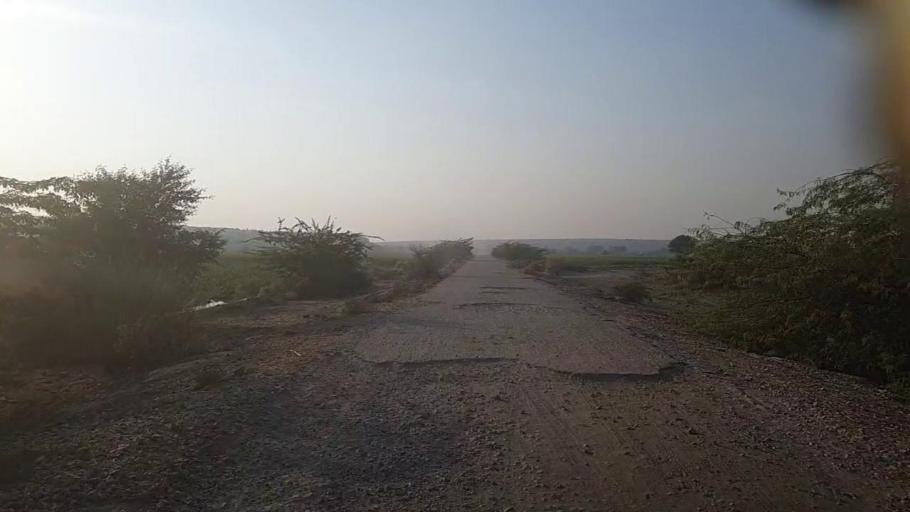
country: PK
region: Sindh
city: Pad Idan
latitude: 26.7218
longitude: 68.4471
